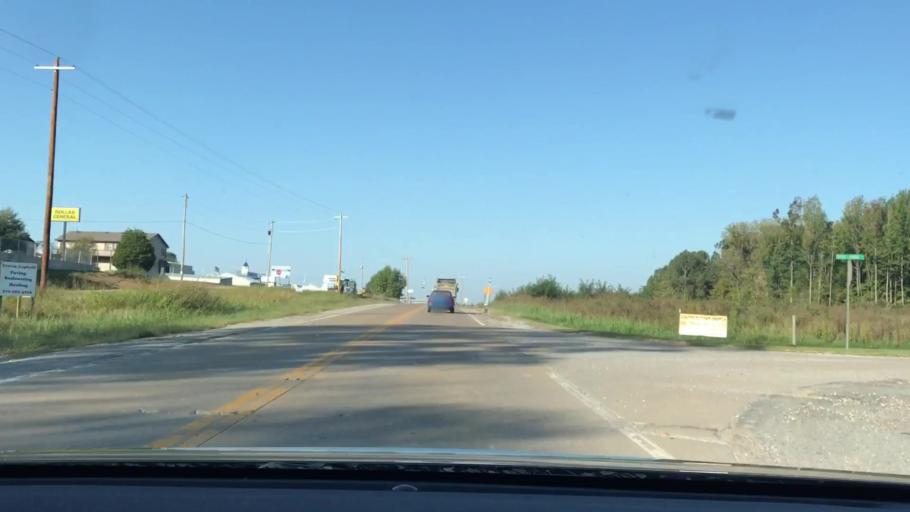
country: US
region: Kentucky
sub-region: Trigg County
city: Cadiz
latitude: 36.7988
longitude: -87.9619
